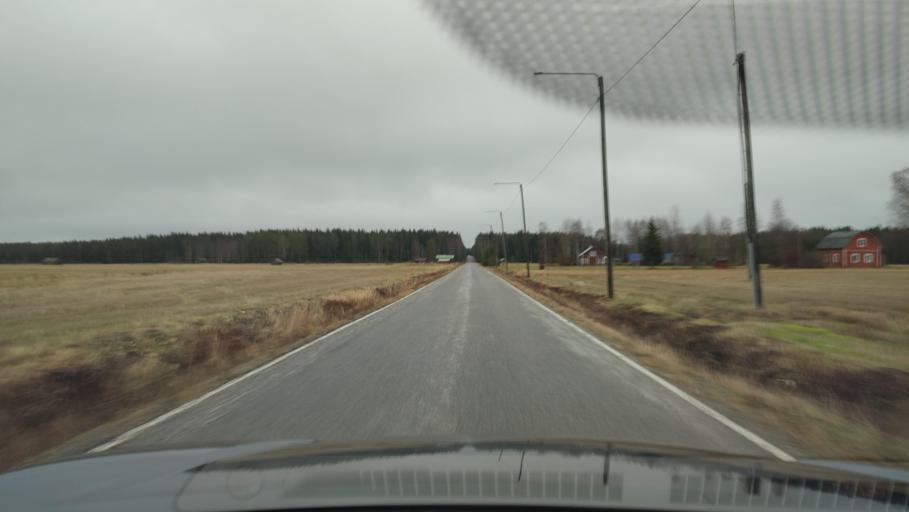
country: FI
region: Southern Ostrobothnia
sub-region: Suupohja
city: Isojoki
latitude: 62.1831
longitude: 21.9286
